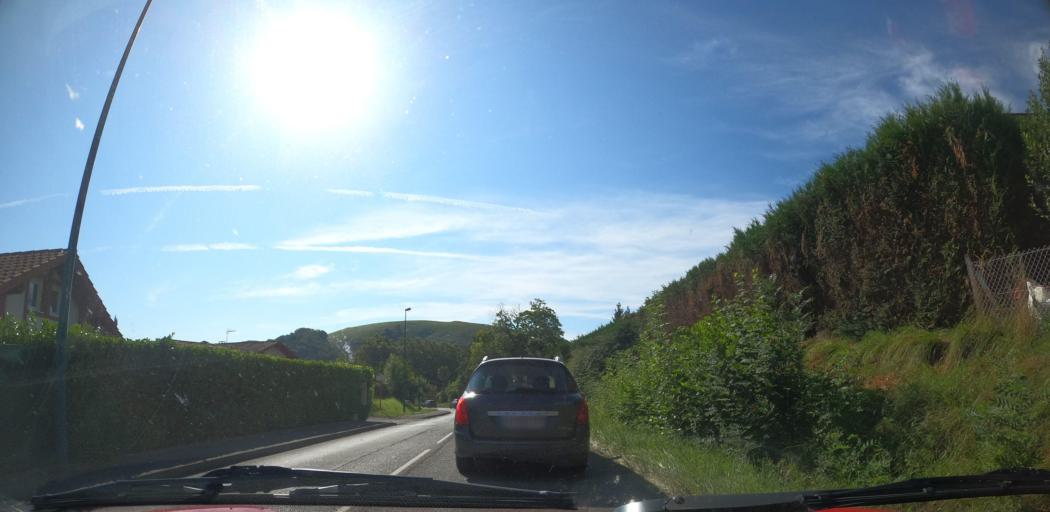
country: FR
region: Aquitaine
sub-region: Departement des Pyrenees-Atlantiques
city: Saint-Pee-sur-Nivelle
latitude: 43.3324
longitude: -1.5473
